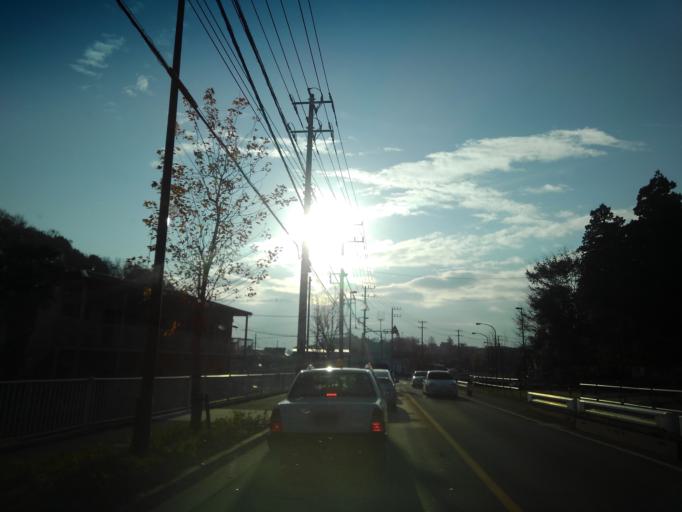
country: JP
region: Tokyo
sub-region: Machida-shi
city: Machida
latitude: 35.5671
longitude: 139.4436
